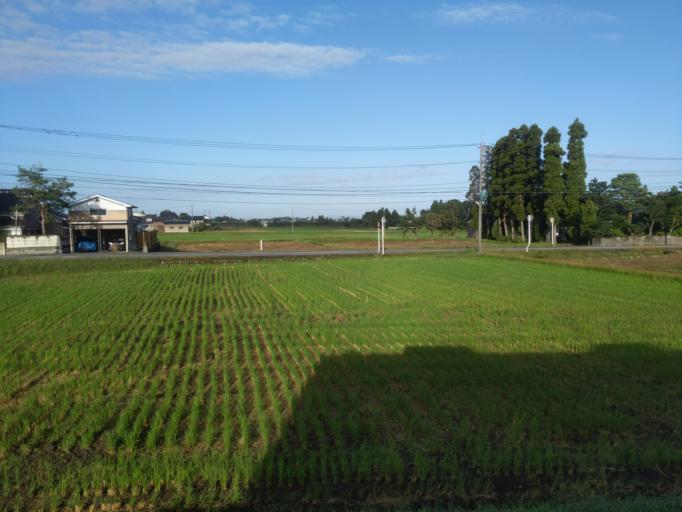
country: JP
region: Toyama
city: Kamiichi
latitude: 36.6734
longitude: 137.3169
